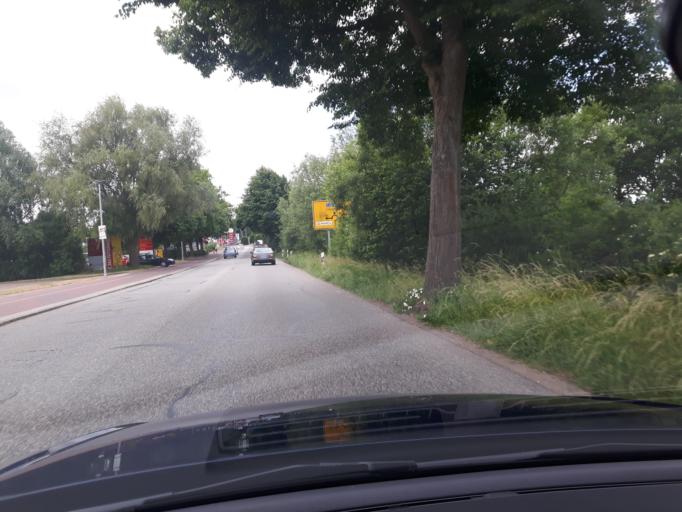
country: DE
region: Schleswig-Holstein
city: Neustadt in Holstein
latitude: 54.1008
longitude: 10.7958
